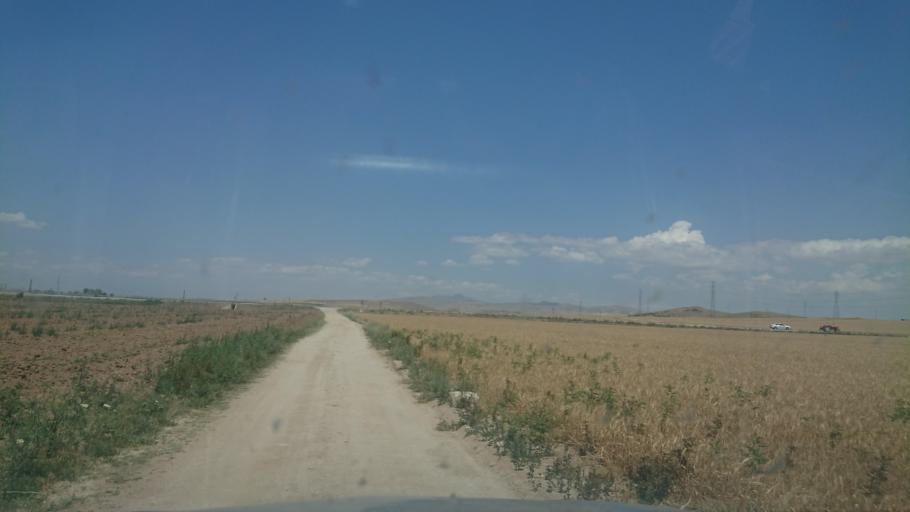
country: TR
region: Aksaray
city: Sariyahsi
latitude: 39.0177
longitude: 33.8743
